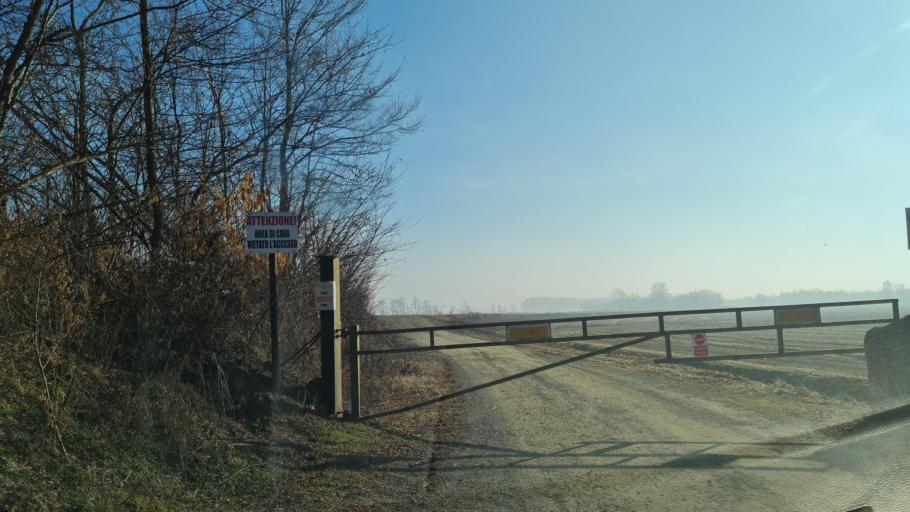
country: IT
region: Piedmont
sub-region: Provincia di Vercelli
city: Buronzo
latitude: 45.4614
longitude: 8.2596
